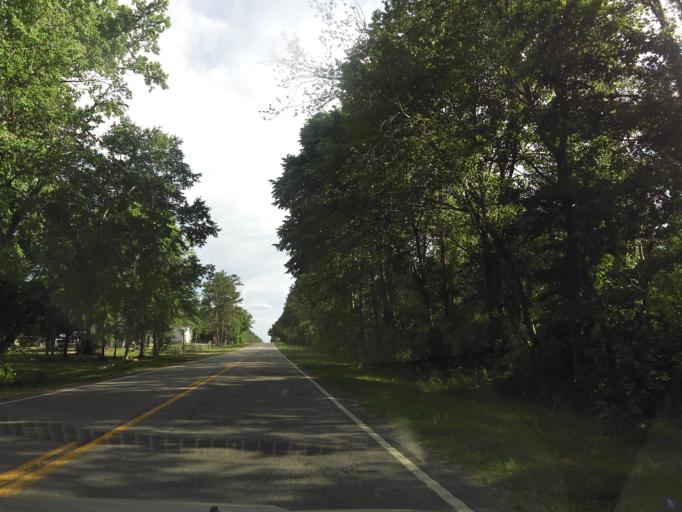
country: US
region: South Carolina
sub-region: Hampton County
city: Estill
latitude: 32.8088
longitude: -81.2401
